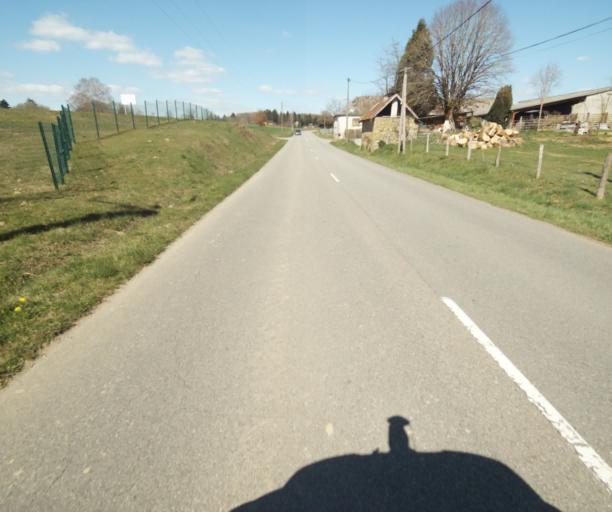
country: FR
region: Limousin
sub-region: Departement de la Correze
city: Saint-Mexant
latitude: 45.2925
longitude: 1.6690
